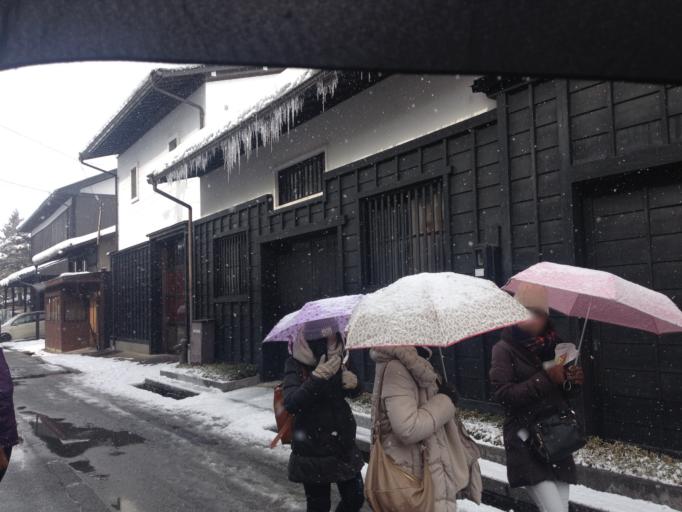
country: JP
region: Gifu
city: Takayama
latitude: 36.2354
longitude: 137.1860
